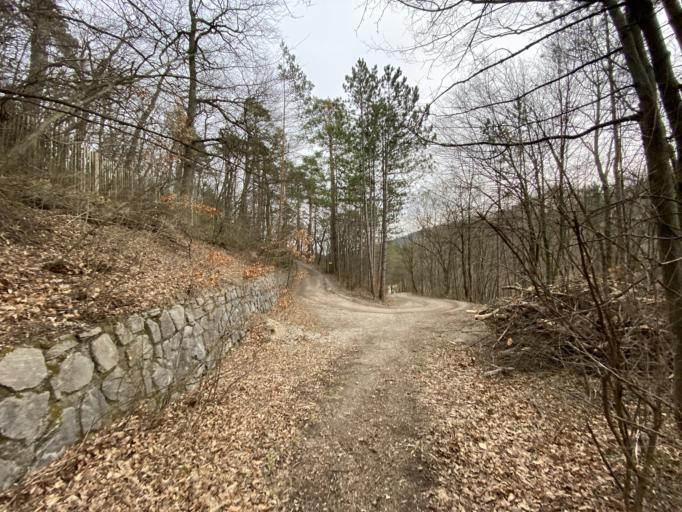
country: AT
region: Lower Austria
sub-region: Politischer Bezirk Modling
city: Gaaden
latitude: 48.0324
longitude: 16.1779
